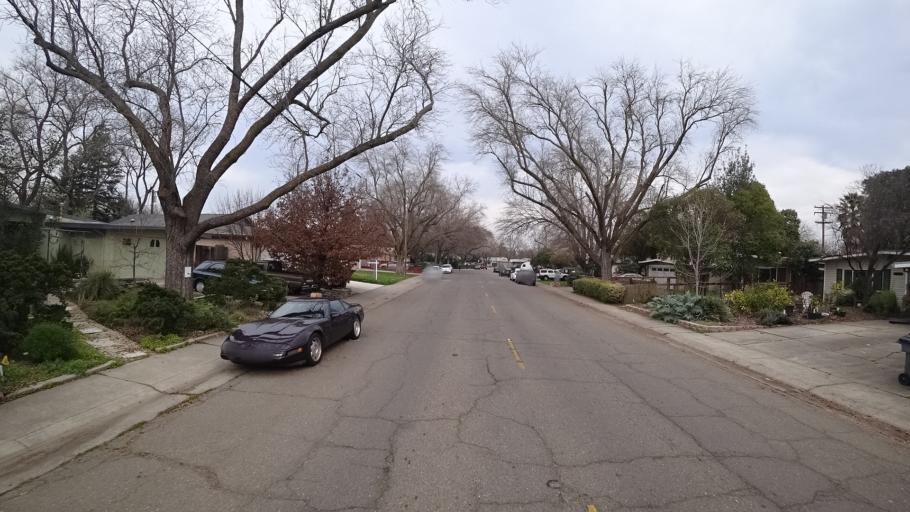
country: US
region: California
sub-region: Yolo County
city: Davis
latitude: 38.5586
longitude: -121.7306
